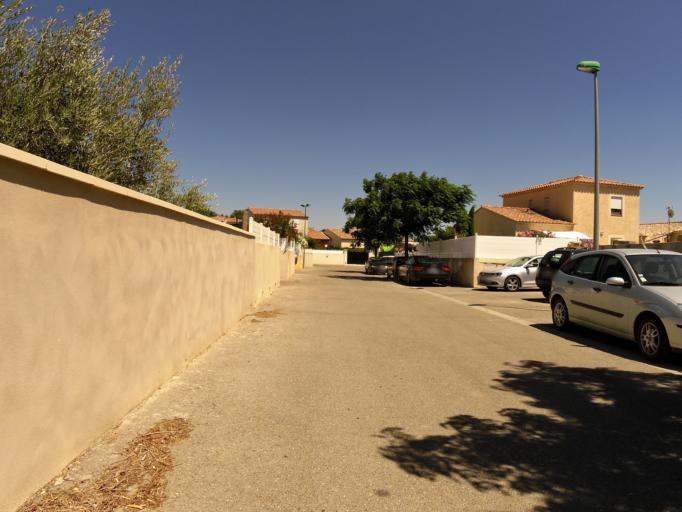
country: FR
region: Languedoc-Roussillon
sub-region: Departement du Gard
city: Clarensac
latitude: 43.8246
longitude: 4.2151
